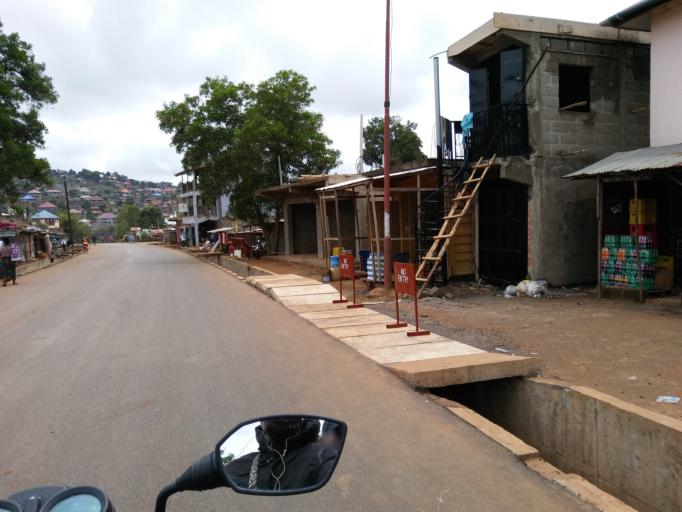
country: SL
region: Western Area
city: Hastings
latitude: 8.3961
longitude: -13.1550
